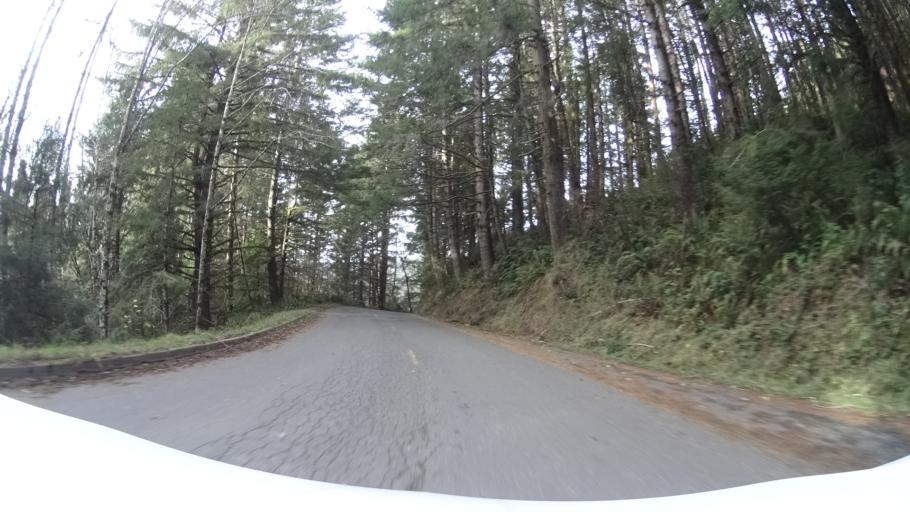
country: US
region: California
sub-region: Humboldt County
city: Ferndale
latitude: 40.5199
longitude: -124.2665
